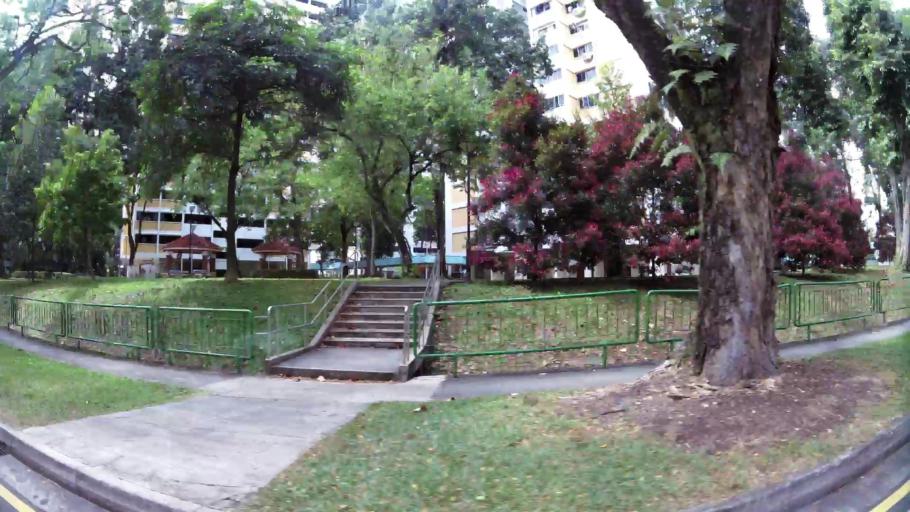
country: SG
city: Singapore
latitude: 1.3169
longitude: 103.7697
